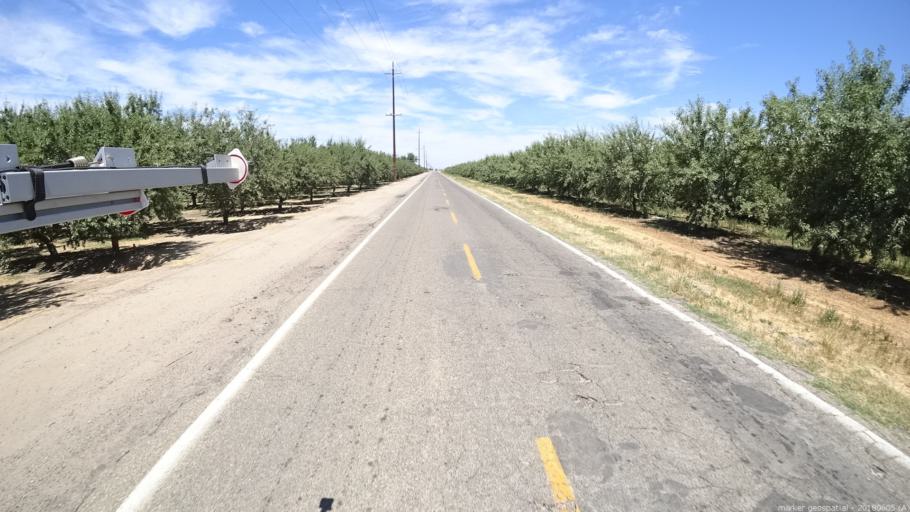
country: US
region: California
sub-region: Madera County
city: Chowchilla
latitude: 37.1240
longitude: -120.3109
